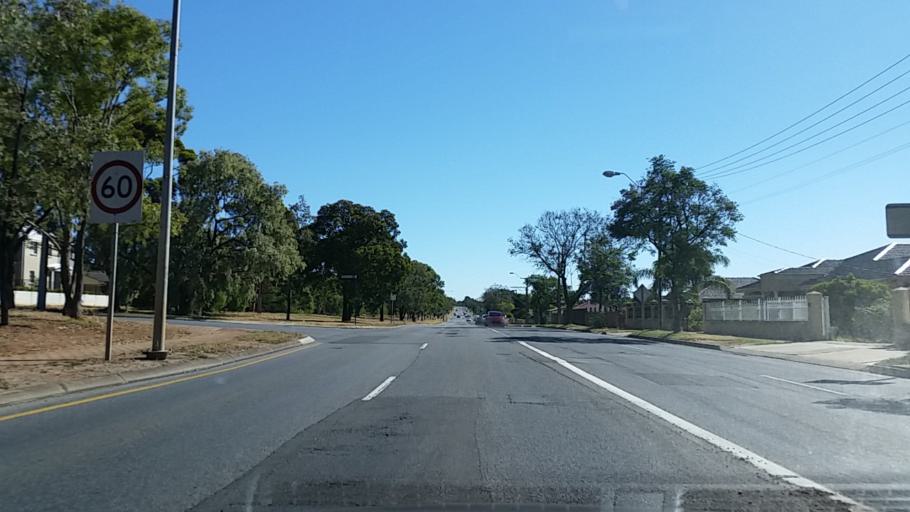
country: AU
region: South Australia
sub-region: Salisbury
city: Ingle Farm
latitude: -34.8253
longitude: 138.6347
